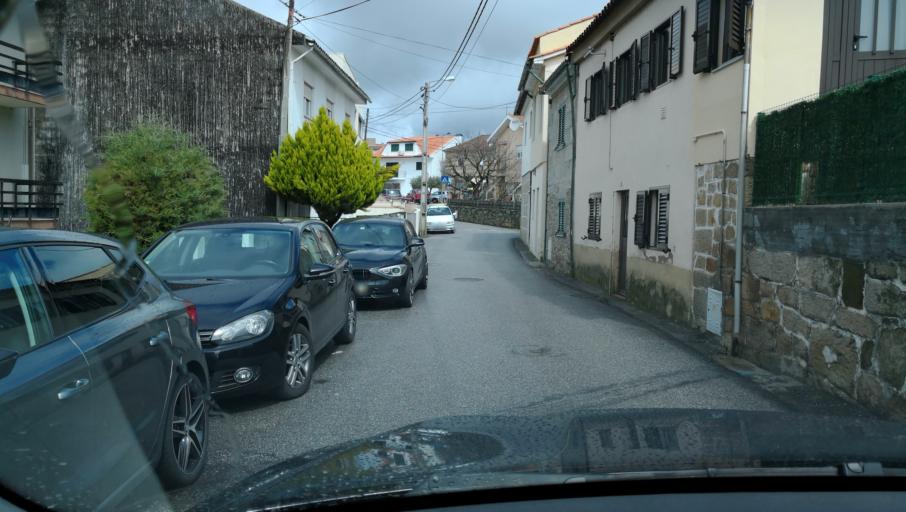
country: PT
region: Vila Real
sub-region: Vila Real
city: Vila Real
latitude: 41.3037
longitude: -7.7207
